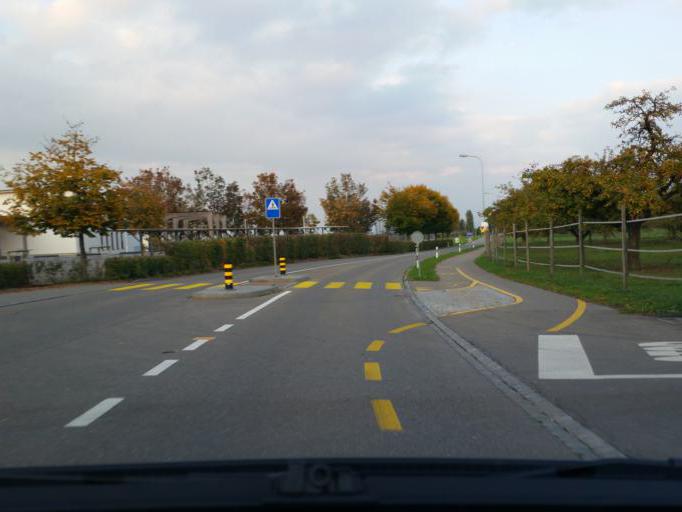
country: CH
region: Thurgau
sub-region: Arbon District
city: Uttwil
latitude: 47.5772
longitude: 9.3220
